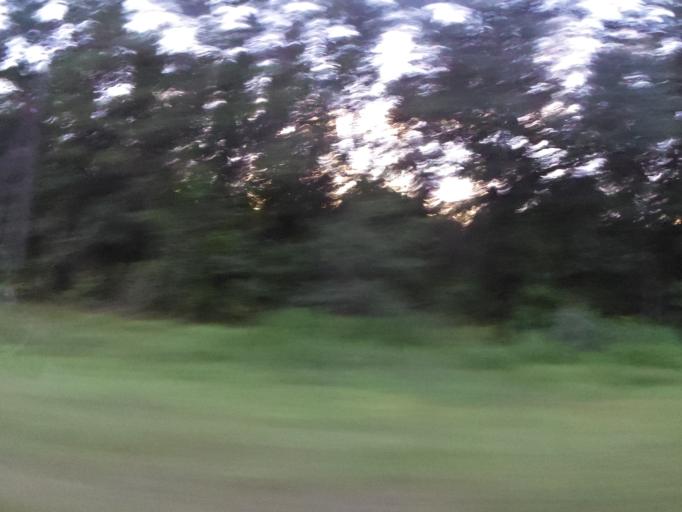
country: US
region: Georgia
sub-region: Camden County
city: Kingsland
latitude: 30.7776
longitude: -81.6868
